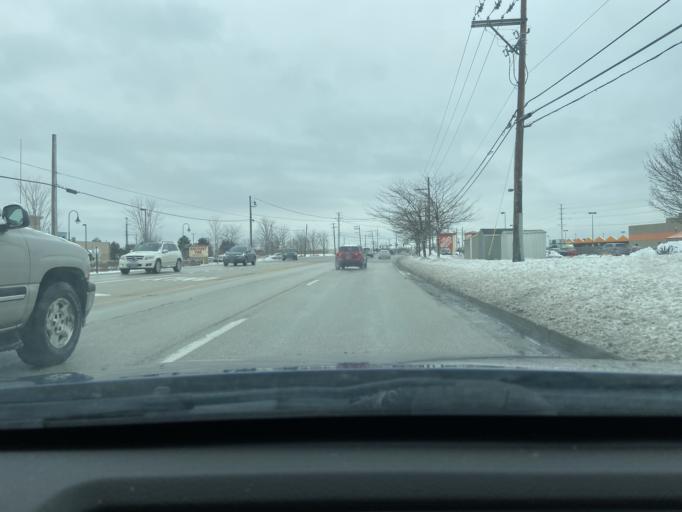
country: US
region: Illinois
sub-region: Lake County
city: Venetian Village
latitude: 42.3865
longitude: -88.0631
